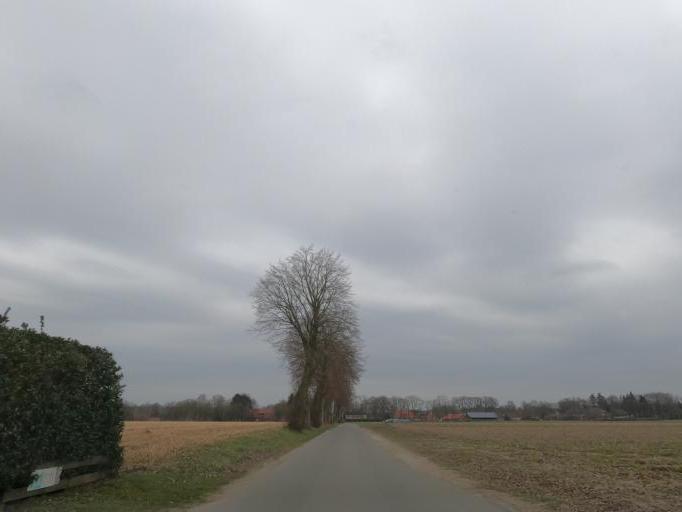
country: DE
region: Lower Saxony
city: Molbergen
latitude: 52.8775
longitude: 7.9078
